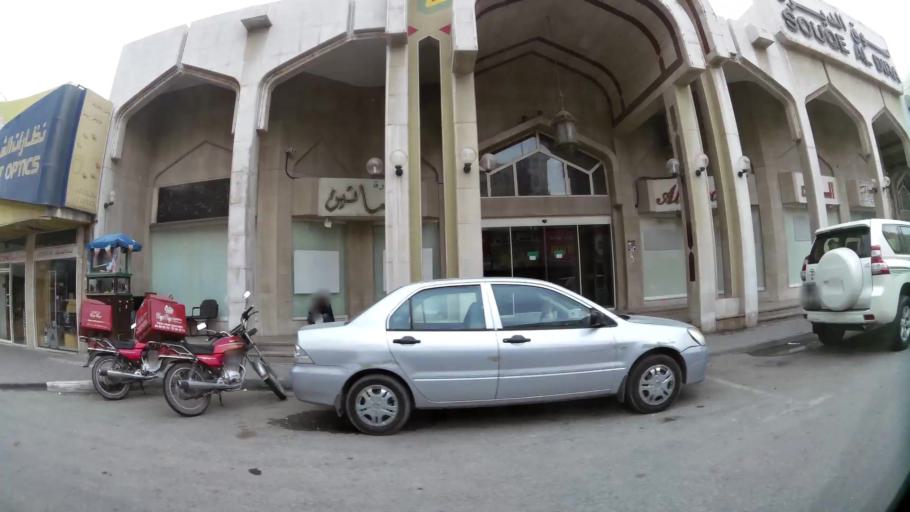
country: QA
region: Baladiyat ad Dawhah
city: Doha
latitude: 25.2886
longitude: 51.5386
